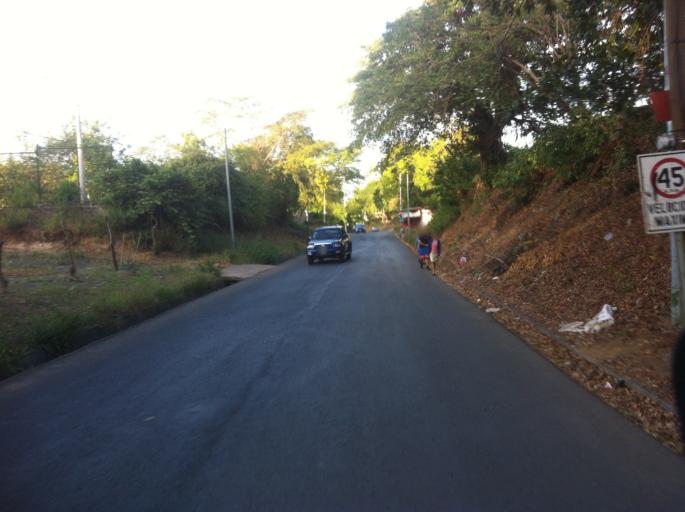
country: NI
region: Managua
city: Managua
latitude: 12.1047
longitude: -86.3010
